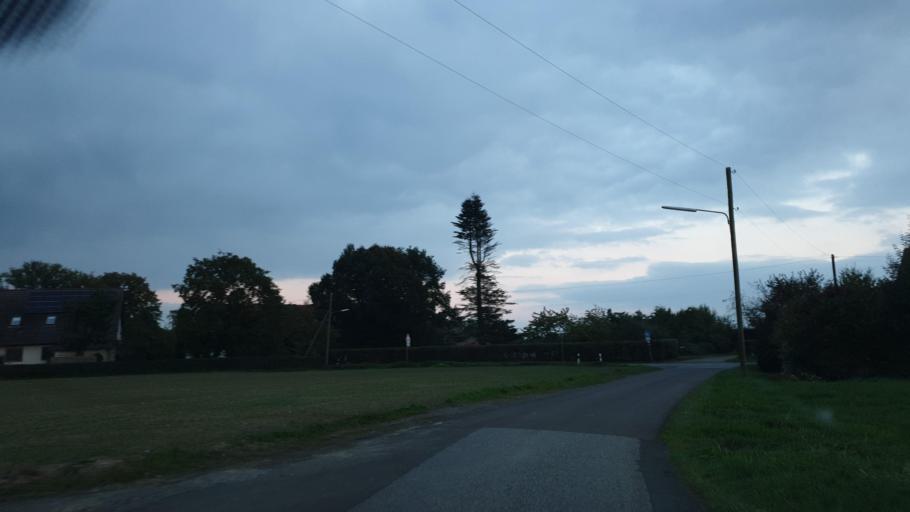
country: DE
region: North Rhine-Westphalia
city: Loehne
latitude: 52.2503
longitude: 8.7340
